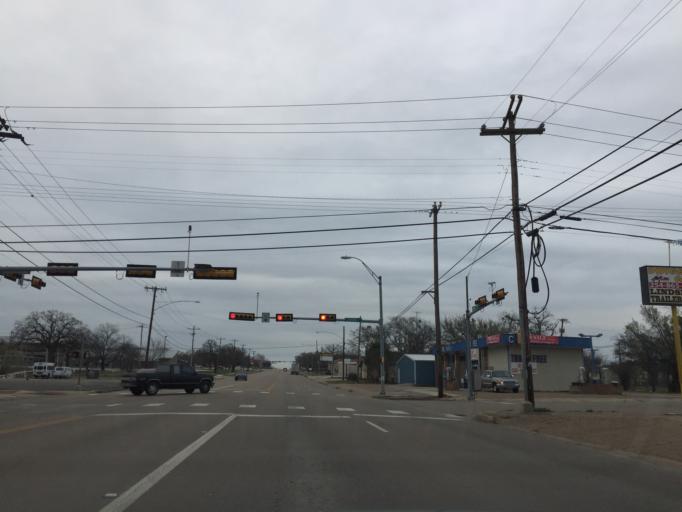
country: US
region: Texas
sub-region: Coryell County
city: Gatesville
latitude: 31.4347
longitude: -97.7256
